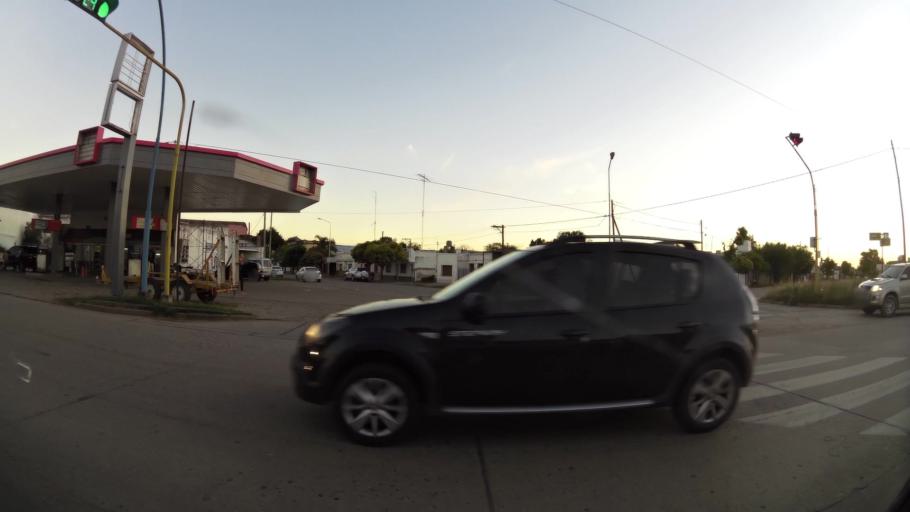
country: AR
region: Cordoba
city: Villa Maria
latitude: -32.4099
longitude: -63.2596
